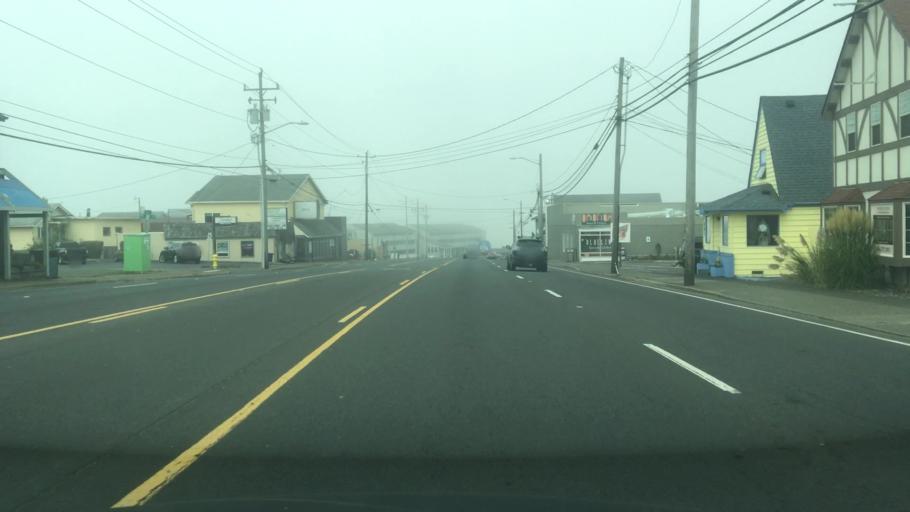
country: US
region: Oregon
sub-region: Lincoln County
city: Lincoln City
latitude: 44.9638
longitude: -124.0175
